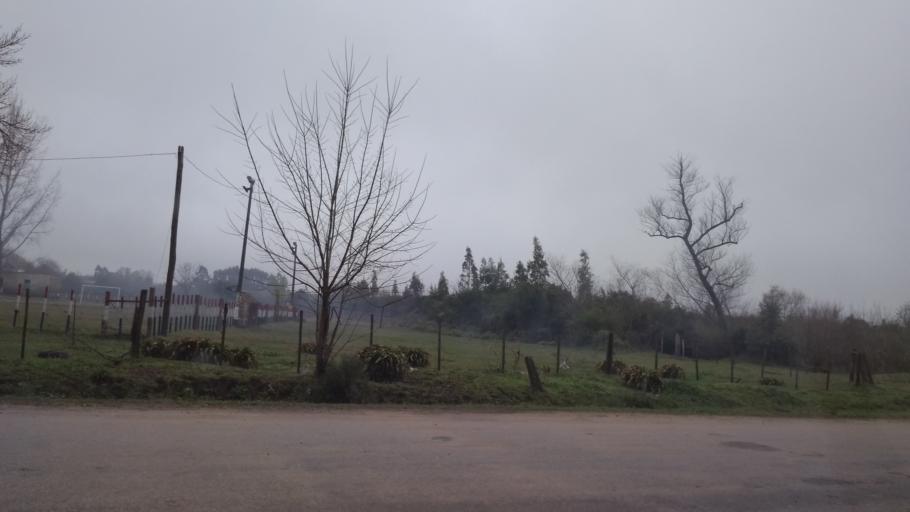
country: UY
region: Florida
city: Florida
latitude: -34.0922
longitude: -56.2070
